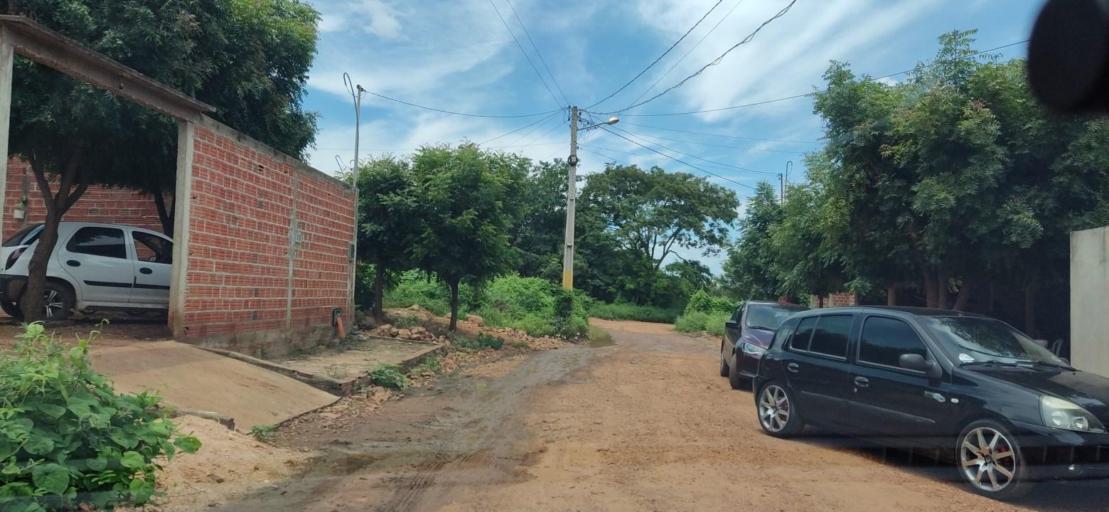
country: BR
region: Piaui
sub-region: Valenca Do Piaui
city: Valenca do Piaui
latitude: -6.4170
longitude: -41.7306
